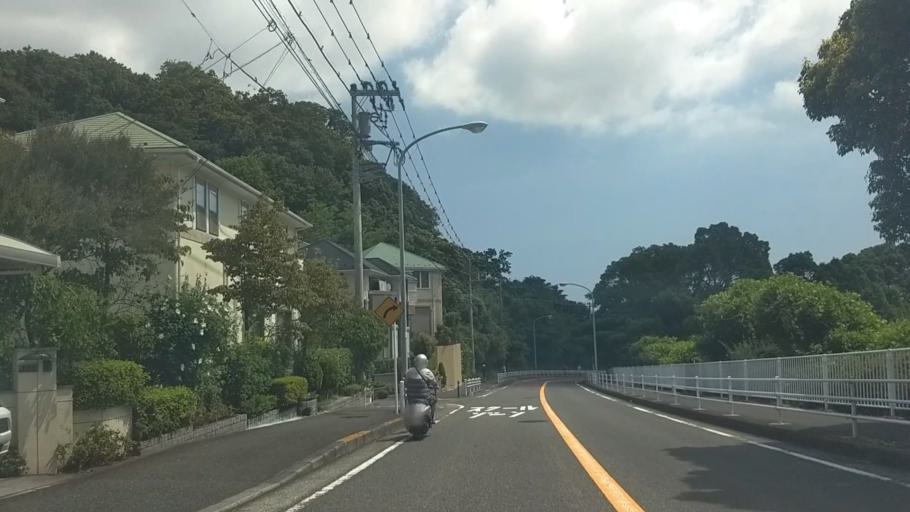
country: JP
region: Kanagawa
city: Yokosuka
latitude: 35.3596
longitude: 139.6338
